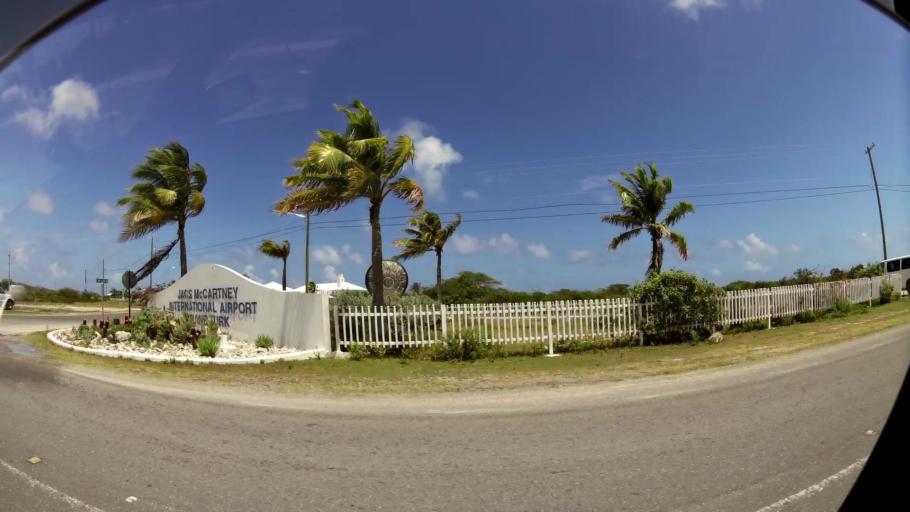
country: TC
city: Cockburn Town
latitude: 21.4409
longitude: -71.1476
